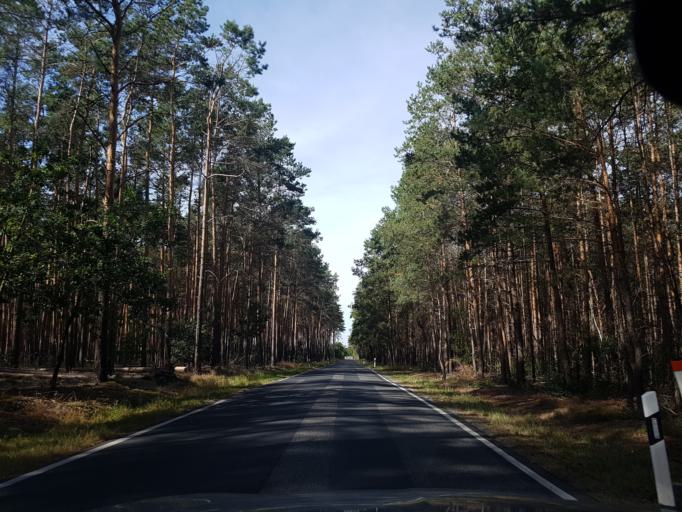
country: DE
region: Brandenburg
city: Schlieben
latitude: 51.6790
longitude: 13.3215
